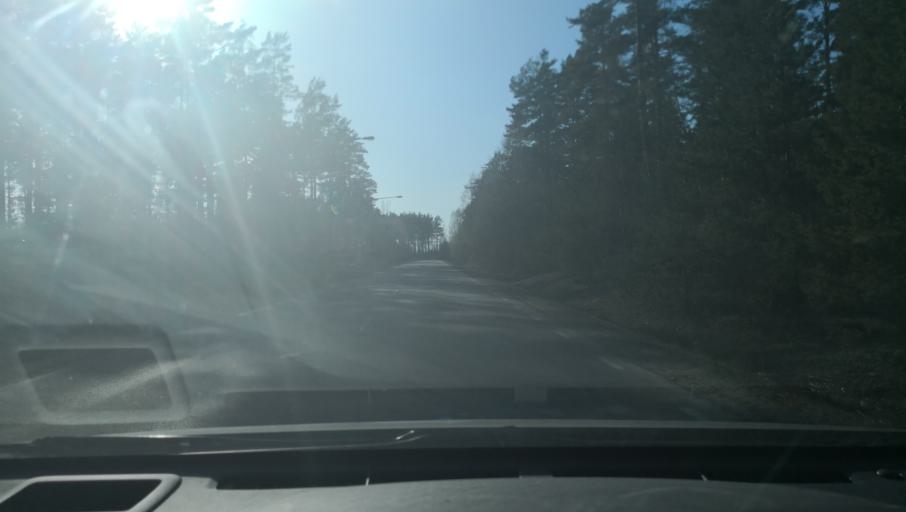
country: SE
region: Uppsala
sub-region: Heby Kommun
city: Tarnsjo
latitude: 60.1543
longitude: 16.9386
